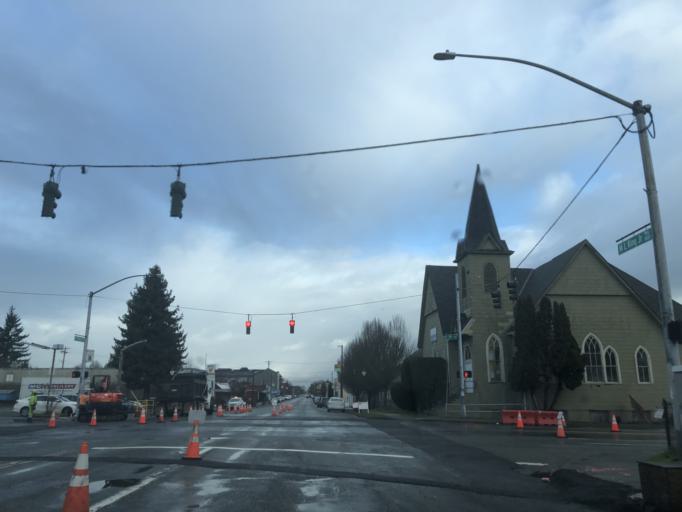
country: US
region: Washington
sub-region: Pierce County
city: Tacoma
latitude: 47.2477
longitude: -122.4507
